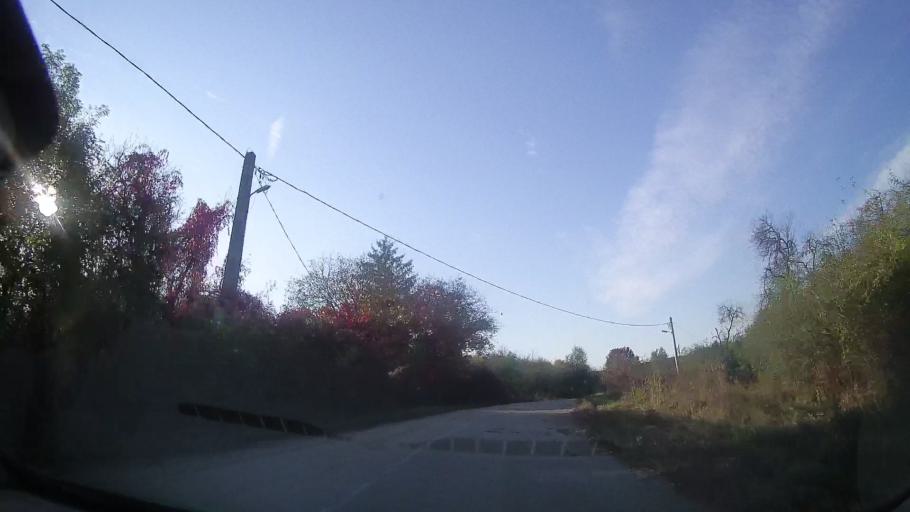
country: RO
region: Timis
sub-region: Comuna Bogda
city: Bogda
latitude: 45.9571
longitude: 21.6151
